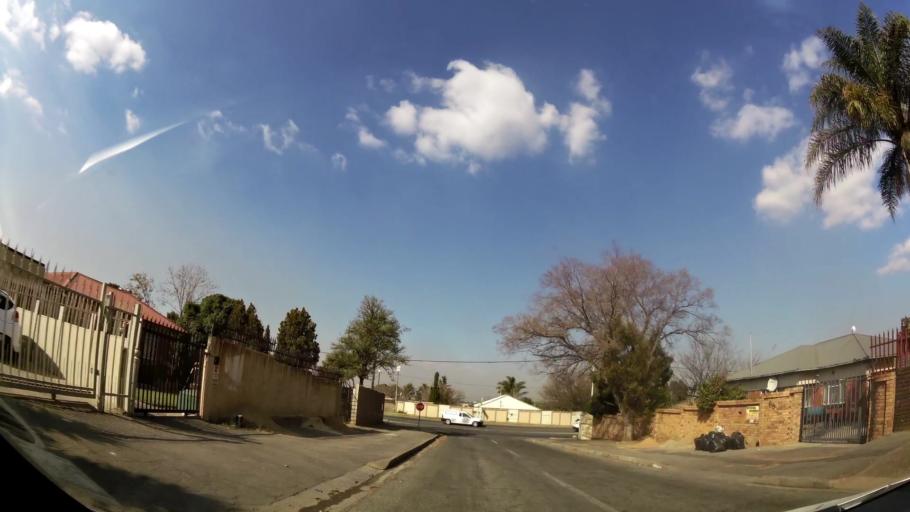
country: ZA
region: Gauteng
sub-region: Ekurhuleni Metropolitan Municipality
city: Germiston
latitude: -26.1789
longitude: 28.1857
